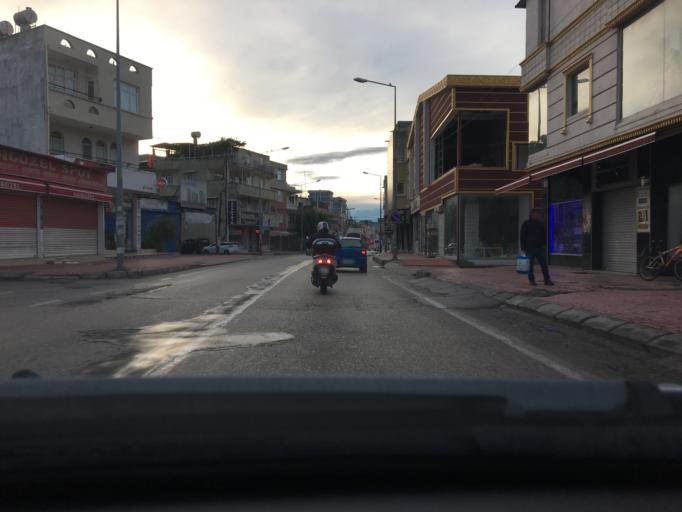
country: TR
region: Adana
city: Seyhan
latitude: 37.0188
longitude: 35.2975
